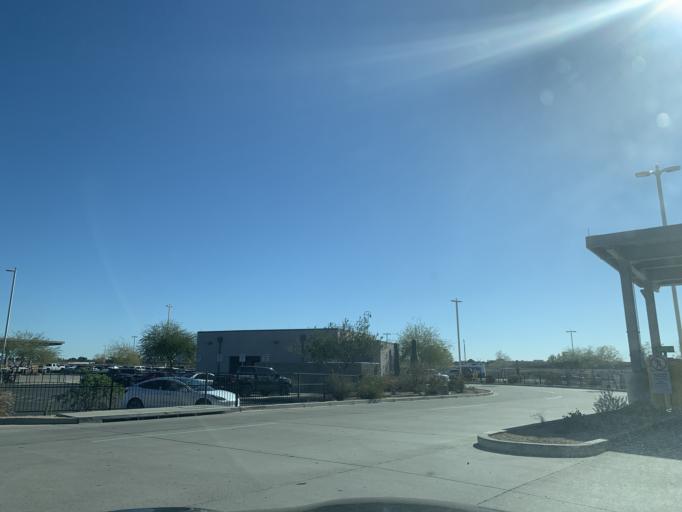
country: US
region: Arizona
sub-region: Maricopa County
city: Tempe Junction
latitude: 33.4332
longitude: -111.9878
